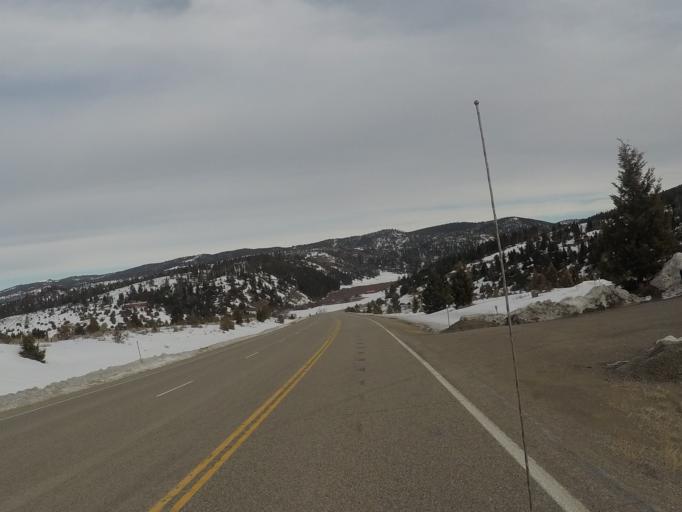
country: US
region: Montana
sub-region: Meagher County
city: White Sulphur Springs
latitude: 46.6631
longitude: -110.8748
